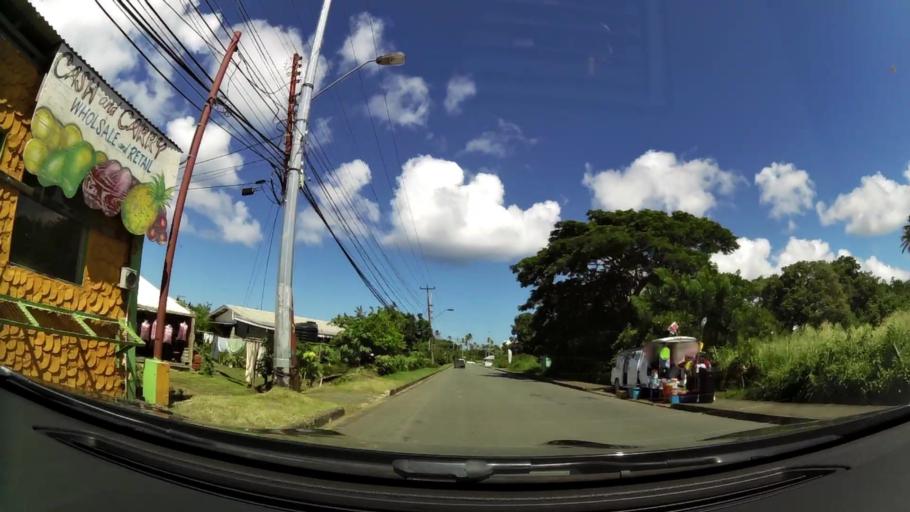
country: TT
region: Tobago
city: Scarborough
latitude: 11.1799
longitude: -60.8009
